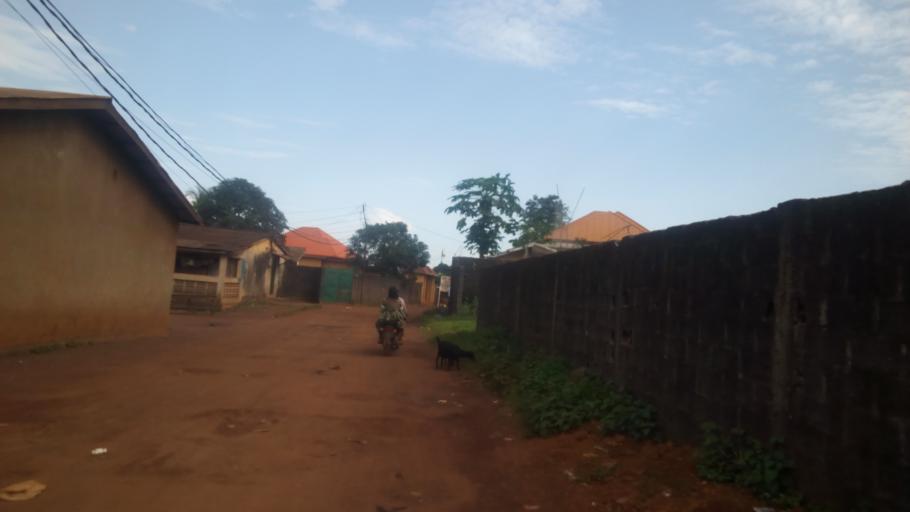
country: GN
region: Kindia
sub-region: Prefecture de Dubreka
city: Dubreka
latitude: 9.6510
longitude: -13.5346
